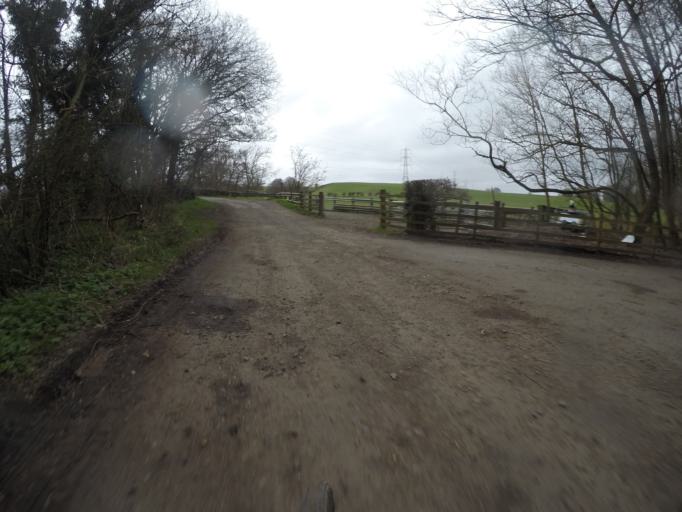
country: GB
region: Scotland
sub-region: East Ayrshire
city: Galston
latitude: 55.6076
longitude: -4.4091
